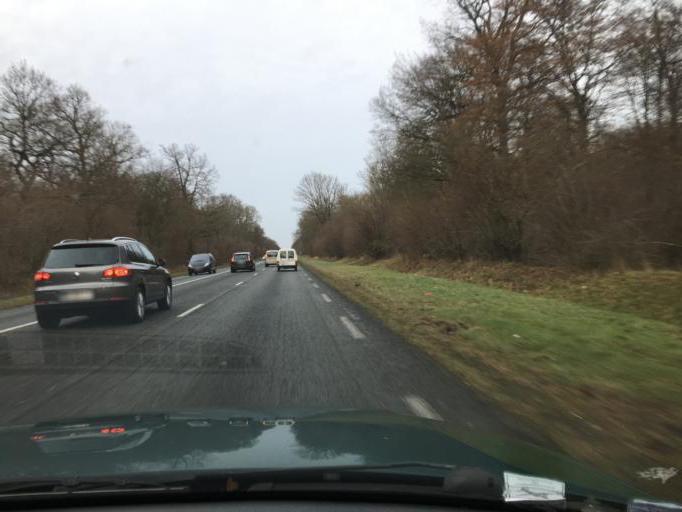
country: FR
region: Picardie
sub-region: Departement de l'Oise
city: Thiers-sur-Theve
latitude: 49.1658
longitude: 2.5565
